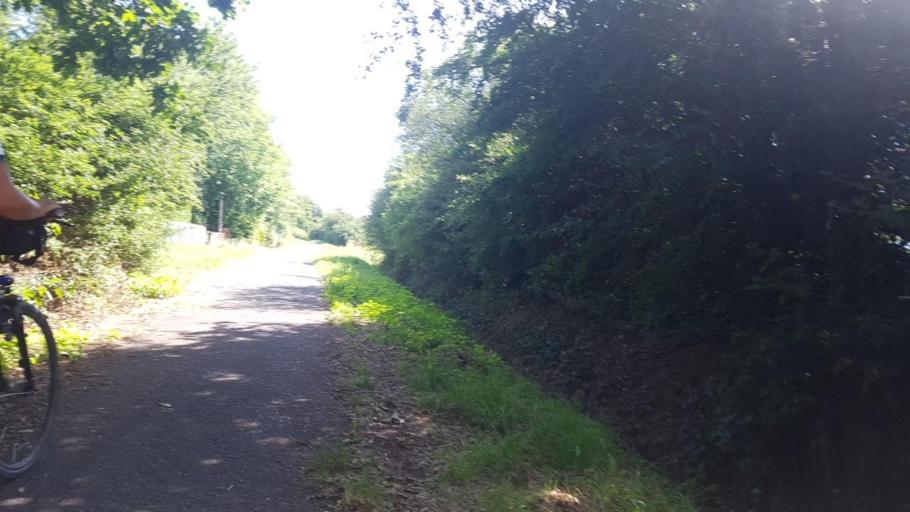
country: DE
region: North Rhine-Westphalia
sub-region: Regierungsbezirk Koln
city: Mechernich
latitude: 50.6359
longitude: 6.7041
